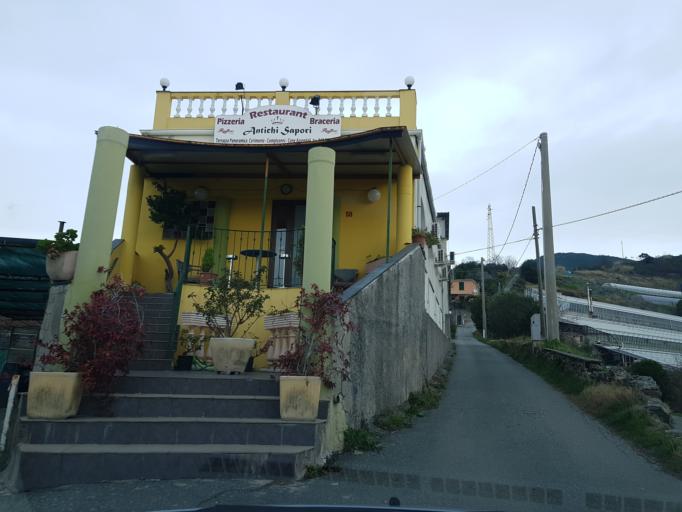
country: IT
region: Liguria
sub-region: Provincia di Genova
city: Mele
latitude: 44.4343
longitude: 8.7975
